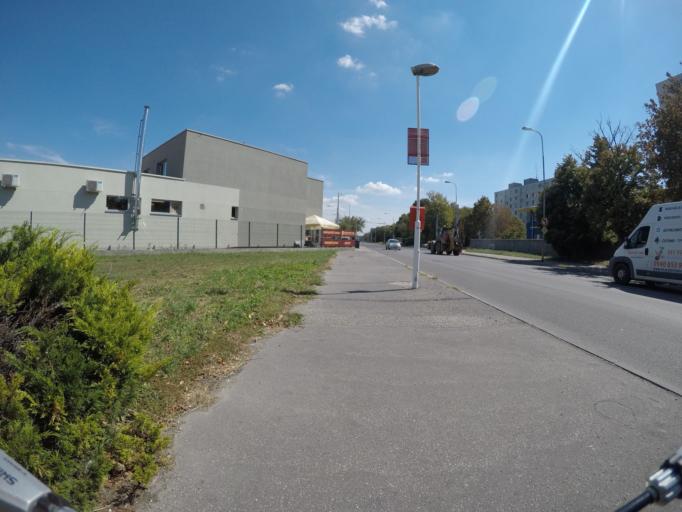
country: SK
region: Bratislavsky
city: Dunajska Luzna
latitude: 48.1456
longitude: 17.2117
